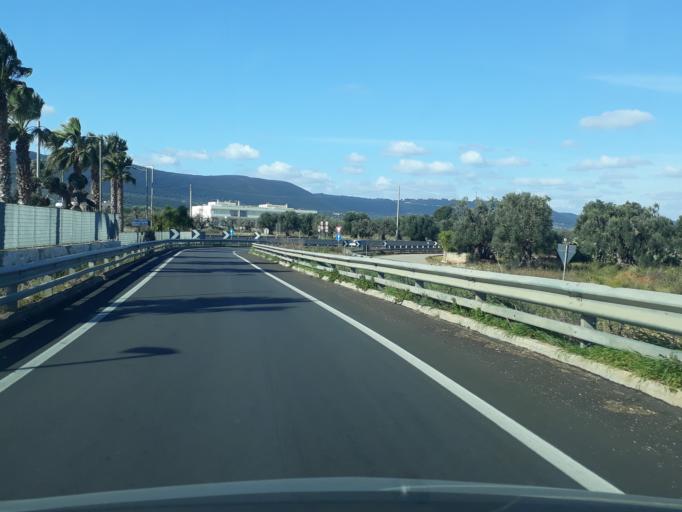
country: IT
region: Apulia
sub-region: Provincia di Brindisi
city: Fasano
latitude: 40.8537
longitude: 17.3558
